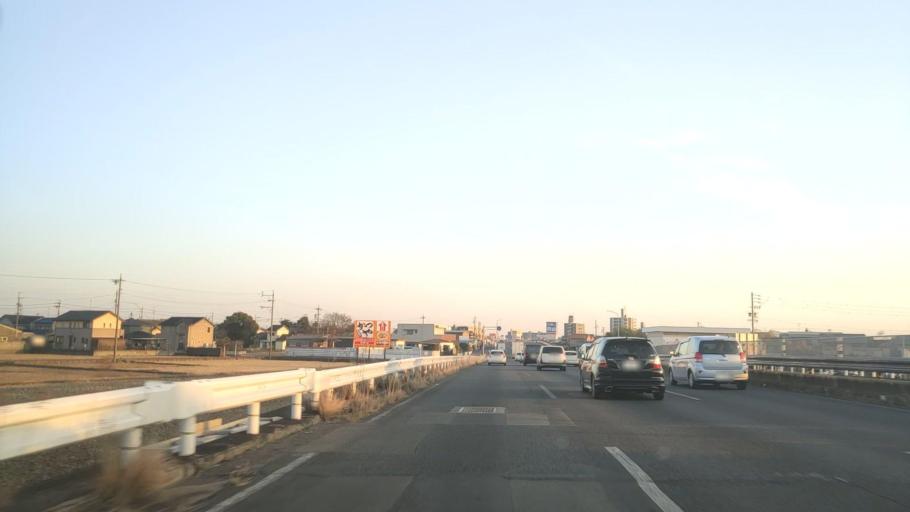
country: JP
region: Aichi
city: Kuroda
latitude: 35.3300
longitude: 136.8043
